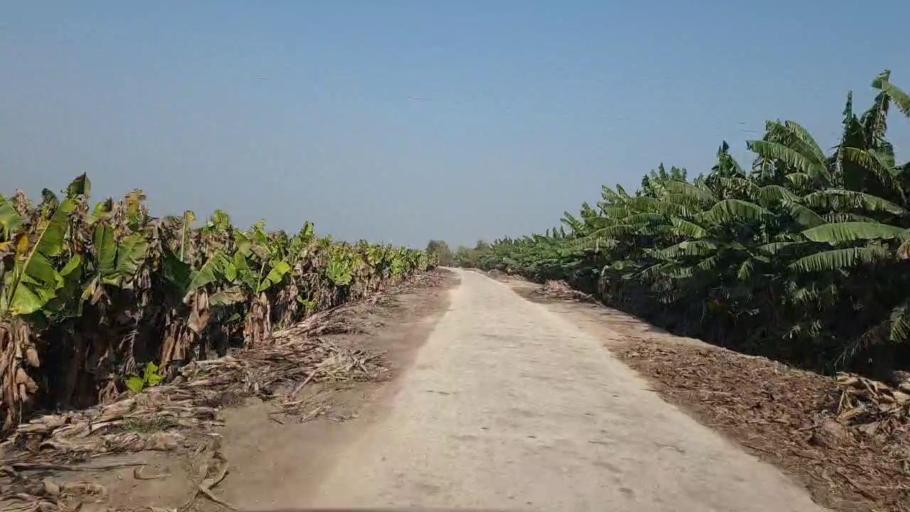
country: PK
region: Sindh
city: Bhit Shah
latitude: 25.7652
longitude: 68.4946
